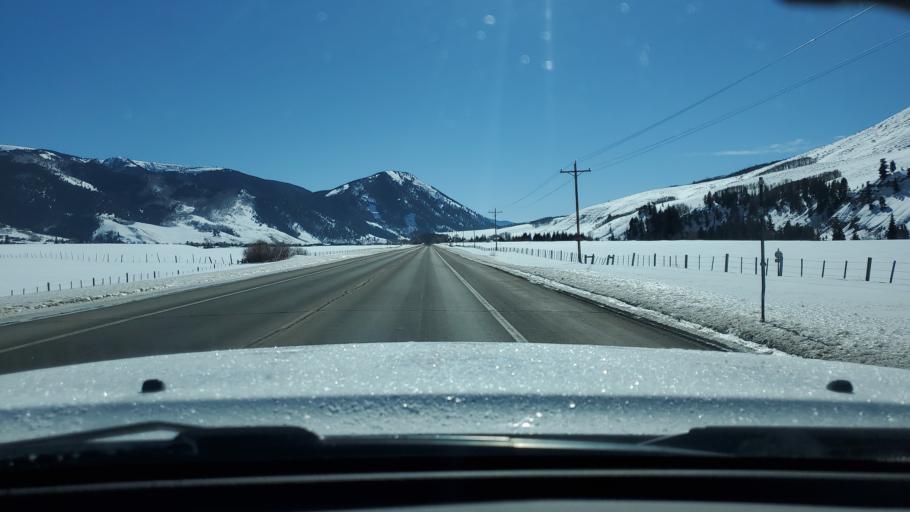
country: US
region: Colorado
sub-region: Gunnison County
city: Crested Butte
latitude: 38.8232
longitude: -106.9160
